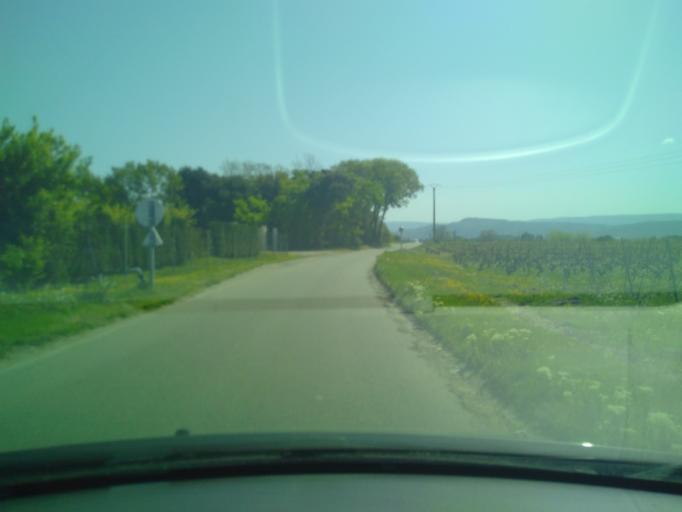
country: FR
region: Provence-Alpes-Cote d'Azur
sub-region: Departement du Vaucluse
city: Mazan
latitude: 44.0652
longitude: 5.1087
